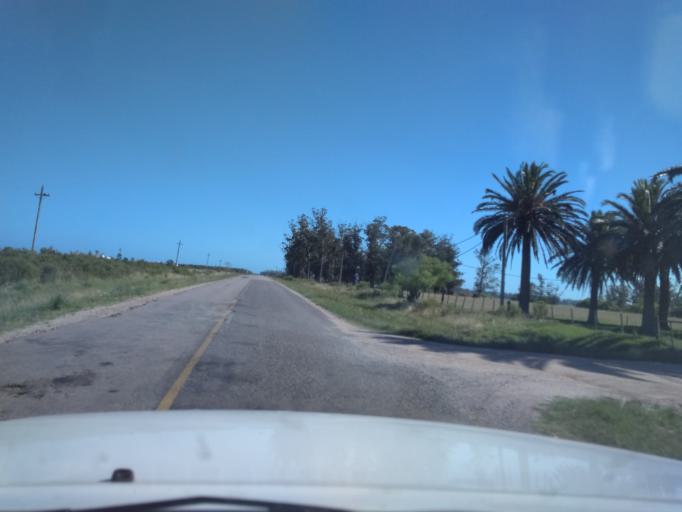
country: UY
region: Canelones
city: San Ramon
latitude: -34.1575
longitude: -55.9467
